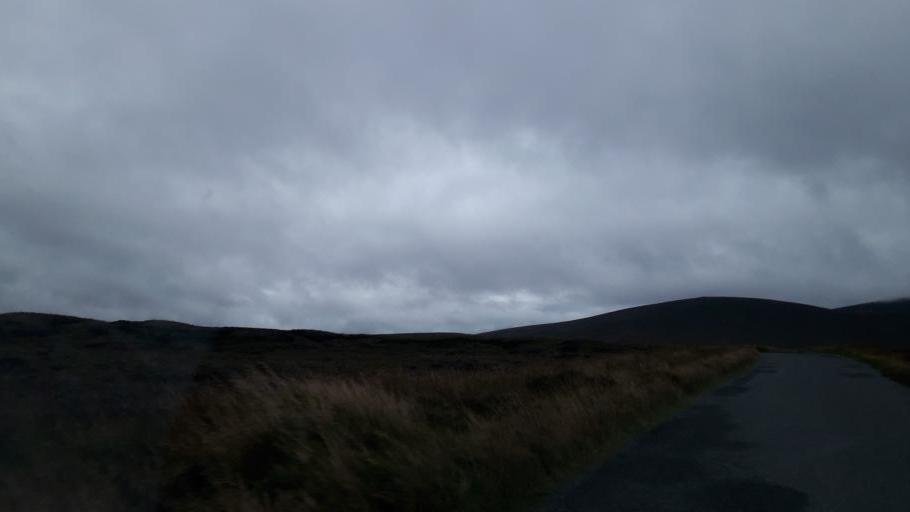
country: IE
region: Leinster
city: Ballyboden
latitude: 53.1593
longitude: -6.3110
